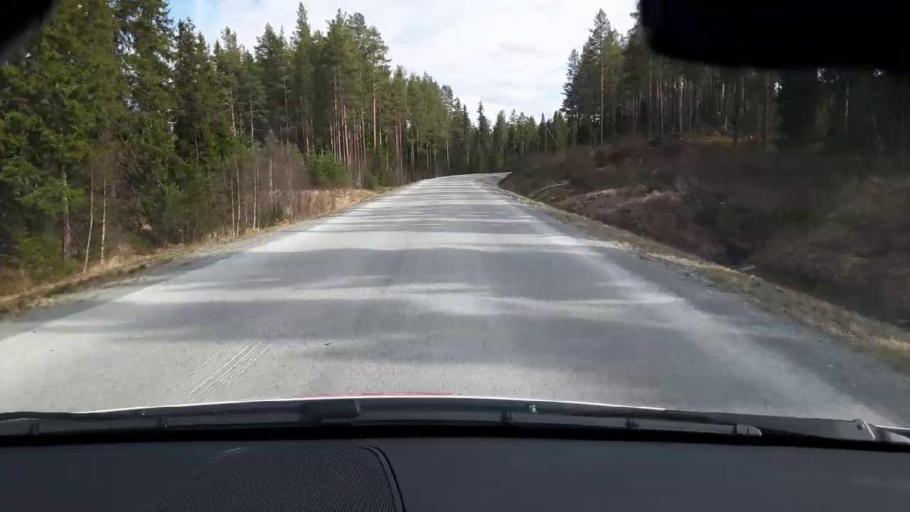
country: SE
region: Jaemtland
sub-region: Bergs Kommun
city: Hoverberg
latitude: 62.7195
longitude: 14.6036
